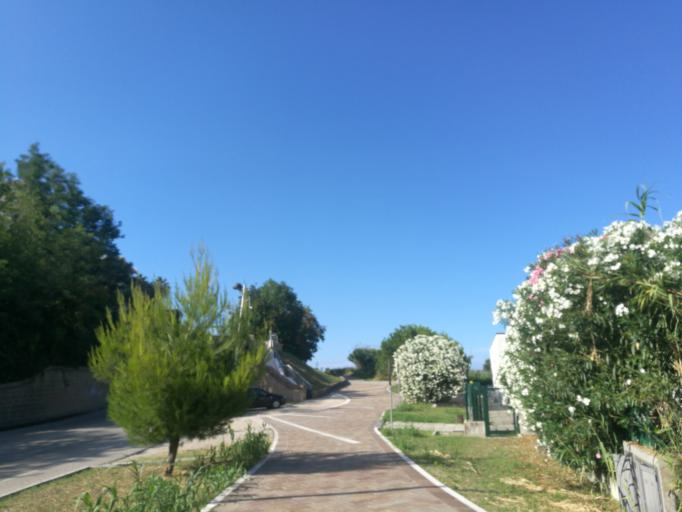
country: IT
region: Molise
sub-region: Provincia di Campobasso
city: Termoli
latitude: 41.9982
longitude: 14.9986
